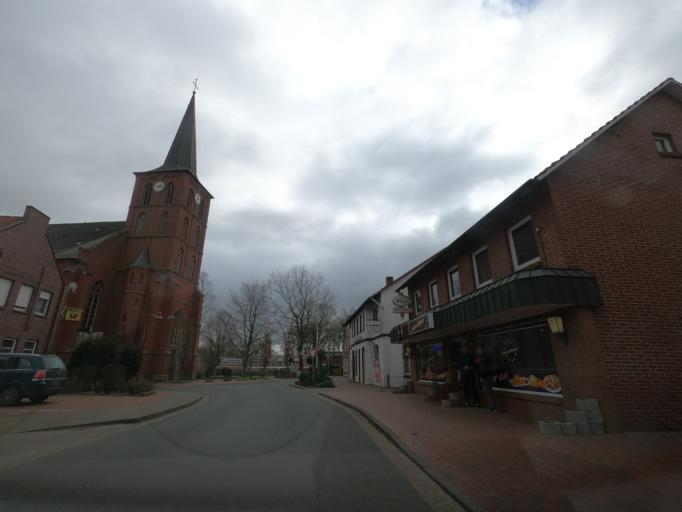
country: DE
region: Lower Saxony
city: Lastrup
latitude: 52.7956
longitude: 7.8638
